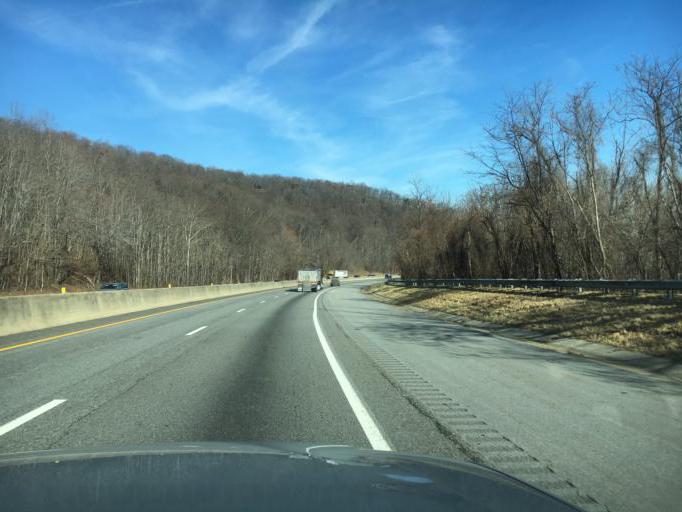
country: US
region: North Carolina
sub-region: Polk County
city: Tryon
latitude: 35.2537
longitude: -82.2458
